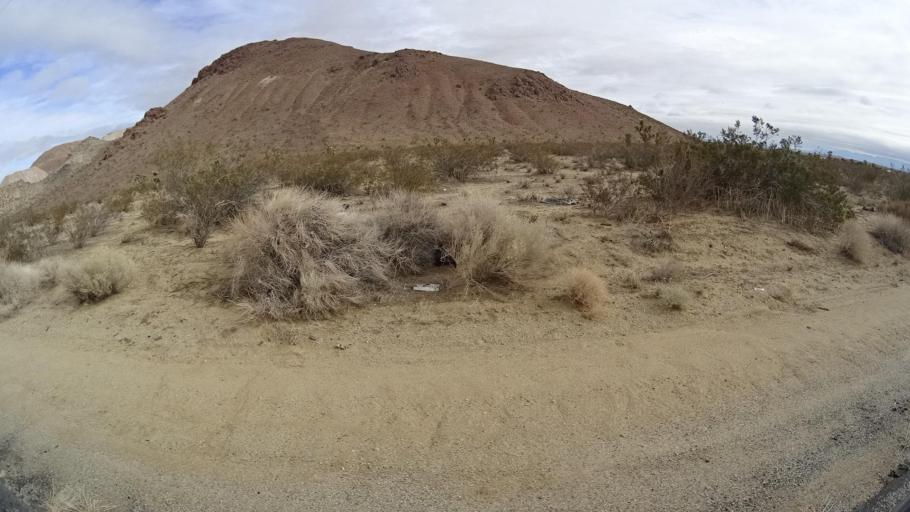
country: US
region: California
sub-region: Kern County
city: Mojave
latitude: 34.9610
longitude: -118.2127
